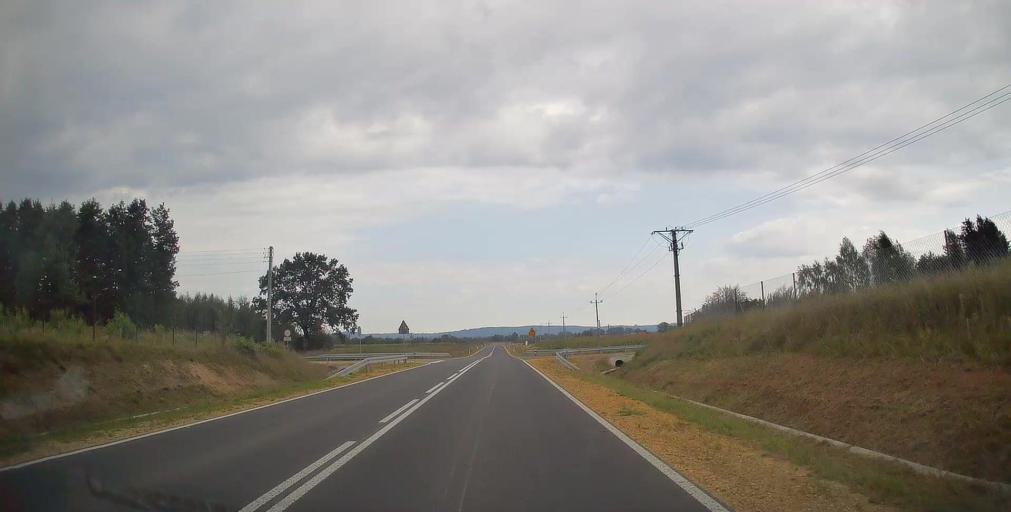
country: PL
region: Lesser Poland Voivodeship
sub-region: Powiat oswiecimski
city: Zator
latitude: 50.0107
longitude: 19.4253
